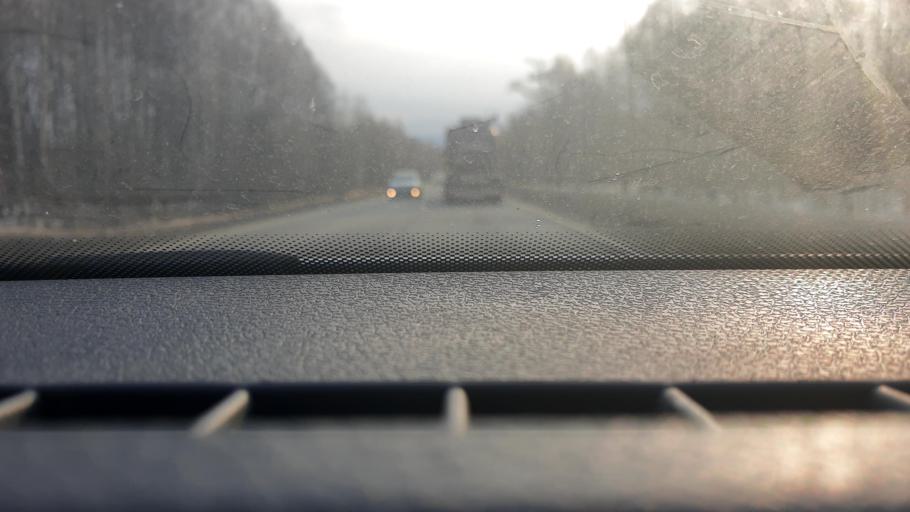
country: RU
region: Chelyabinsk
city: Asha
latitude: 54.8839
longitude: 57.2725
